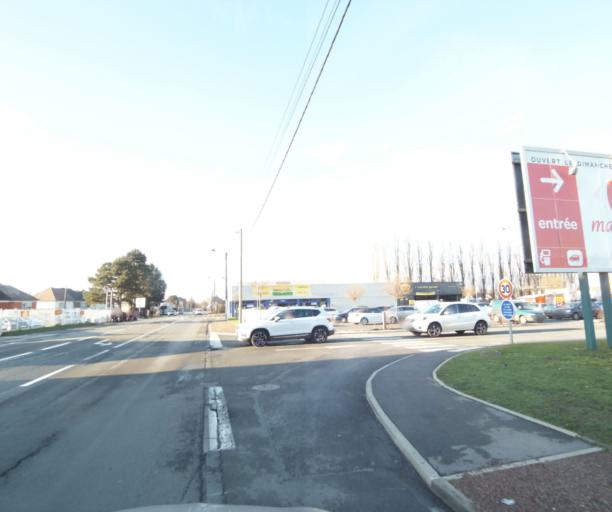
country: FR
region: Nord-Pas-de-Calais
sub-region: Departement du Nord
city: Marly
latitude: 50.3466
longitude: 3.5528
